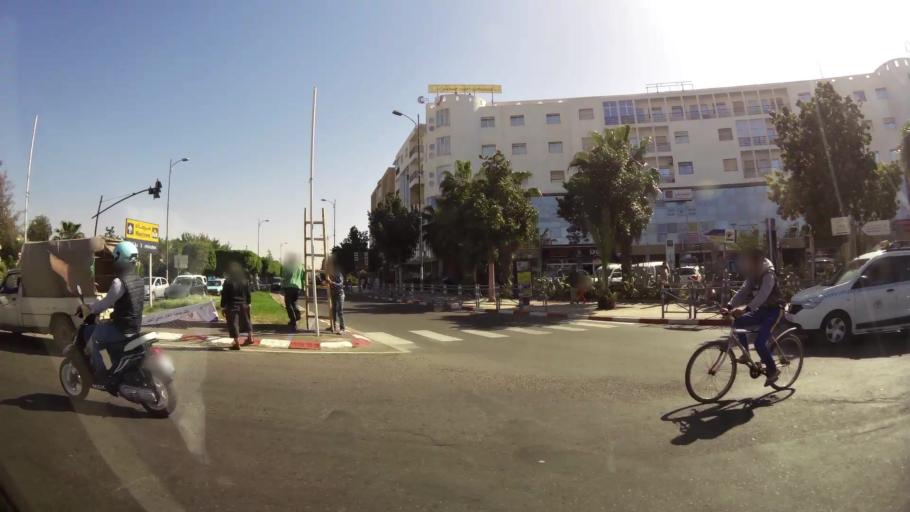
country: MA
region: Souss-Massa-Draa
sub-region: Inezgane-Ait Mellou
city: Inezgane
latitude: 30.3624
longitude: -9.5336
